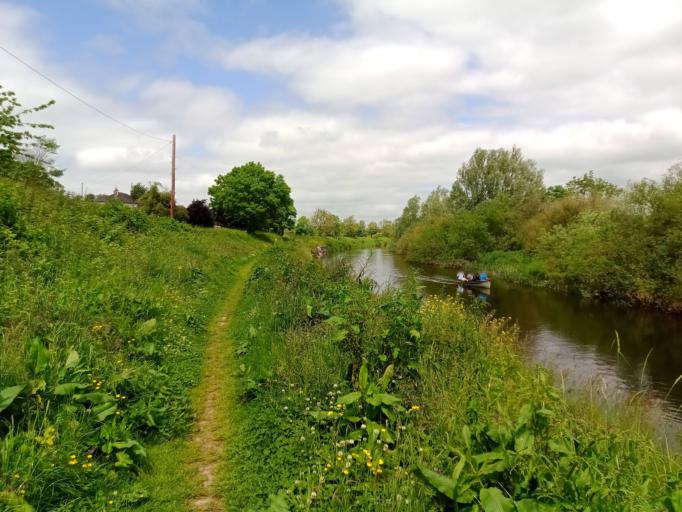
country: IE
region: Leinster
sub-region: County Carlow
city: Carlow
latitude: 52.8059
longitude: -6.9668
